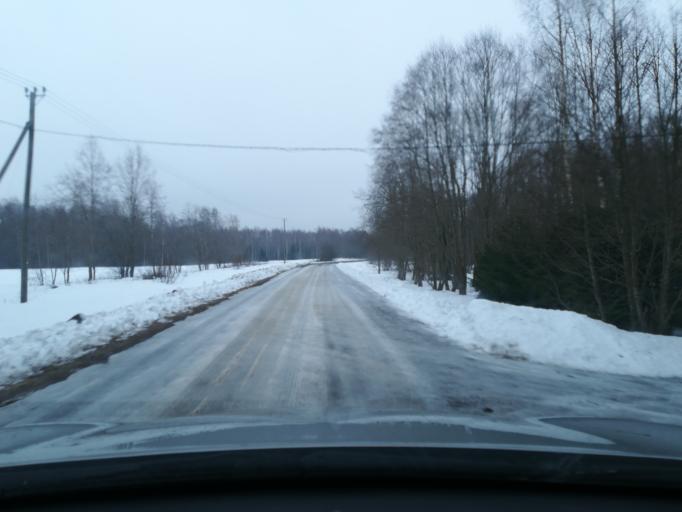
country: EE
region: Harju
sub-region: Loksa linn
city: Loksa
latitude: 59.4685
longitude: 25.6982
